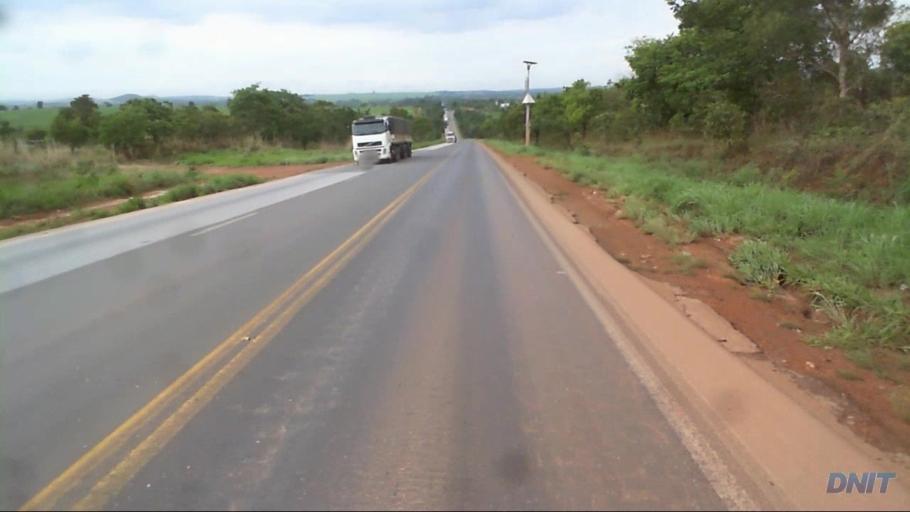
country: BR
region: Goias
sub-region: Uruacu
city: Uruacu
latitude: -14.5750
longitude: -49.1579
